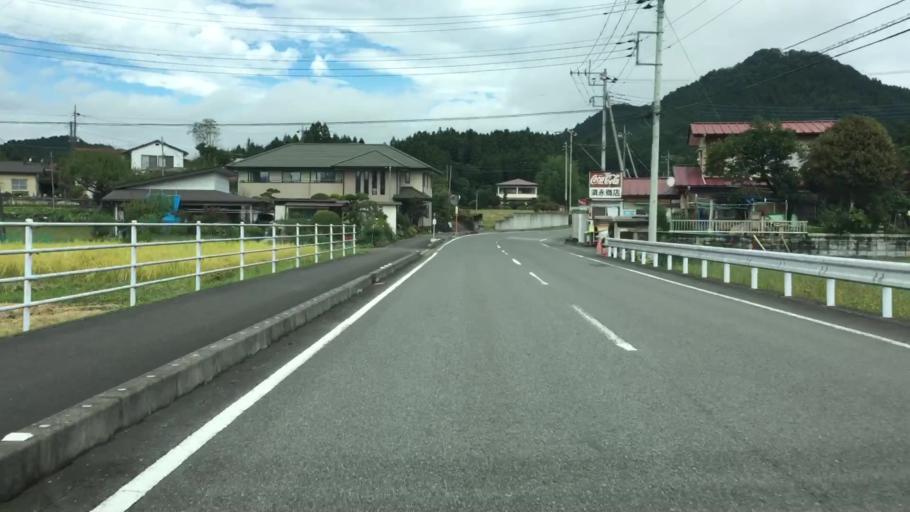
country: JP
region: Tochigi
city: Imaichi
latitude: 36.7440
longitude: 139.6846
